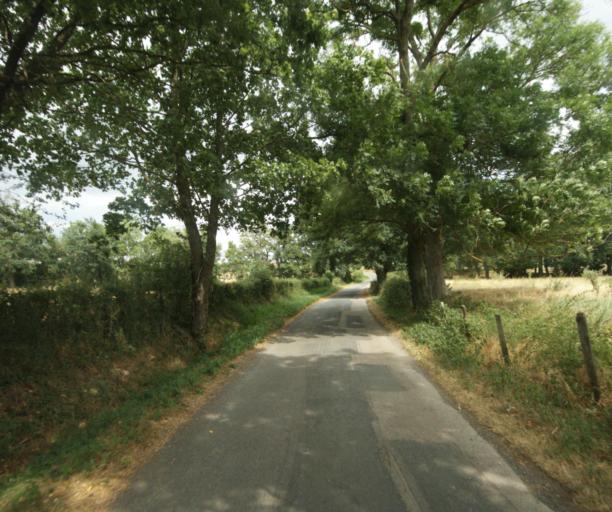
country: FR
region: Rhone-Alpes
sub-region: Departement du Rhone
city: Saint-Romain-de-Popey
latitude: 45.8826
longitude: 4.5345
